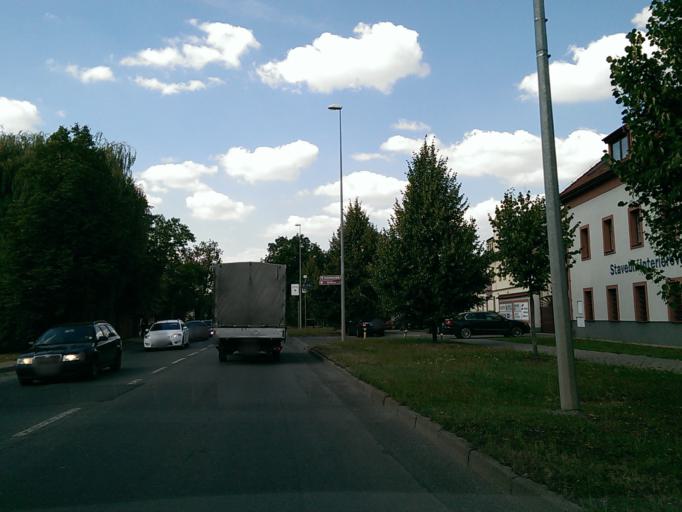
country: CZ
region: Praha
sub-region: Praha 14
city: Dolni Pocernice
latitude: 50.0559
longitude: 14.5626
